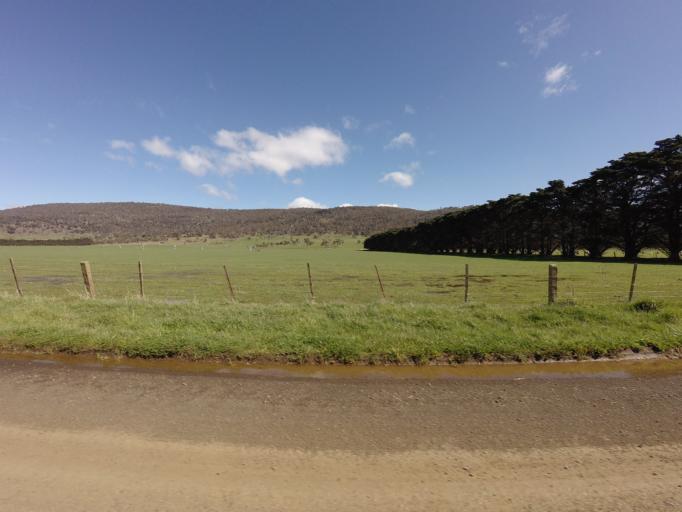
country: AU
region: Tasmania
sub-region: Northern Midlands
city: Evandale
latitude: -41.9578
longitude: 147.4370
